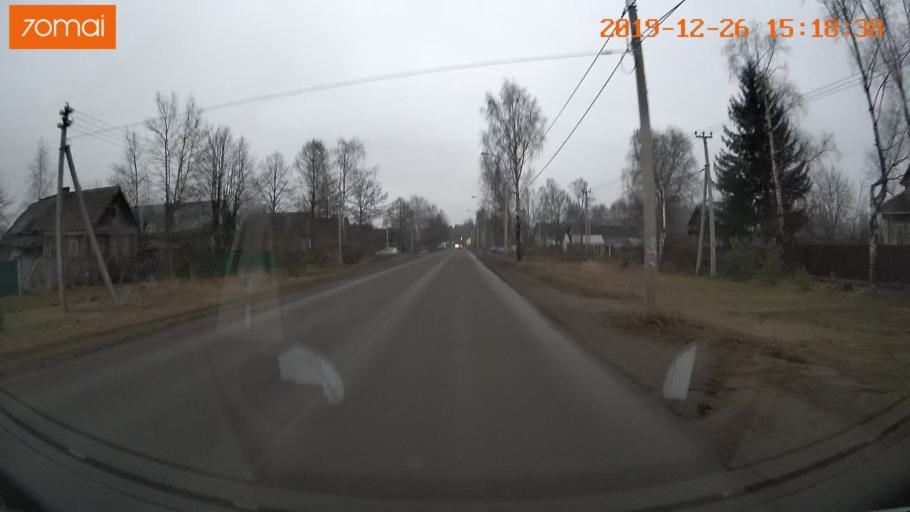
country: RU
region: Jaroslavl
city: Rybinsk
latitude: 58.0698
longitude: 38.8444
